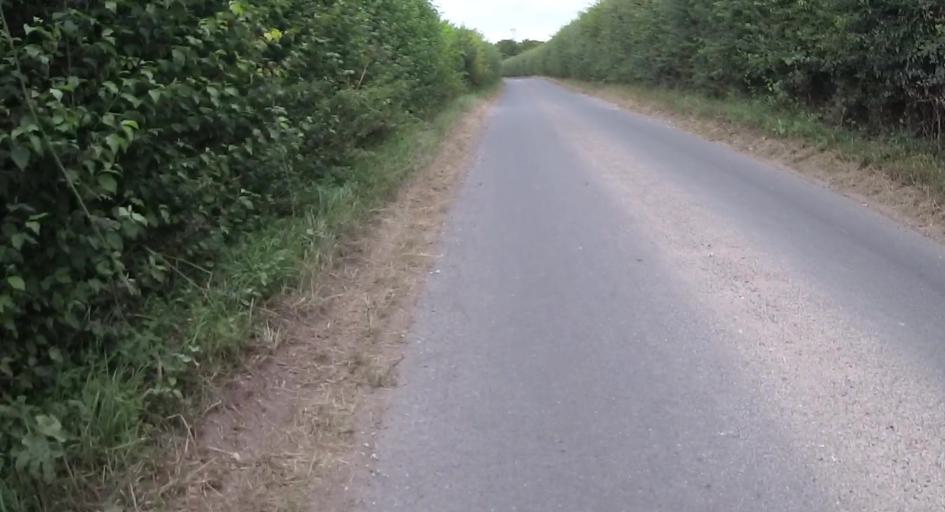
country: GB
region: England
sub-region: Hampshire
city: Overton
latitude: 51.1709
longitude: -1.2945
